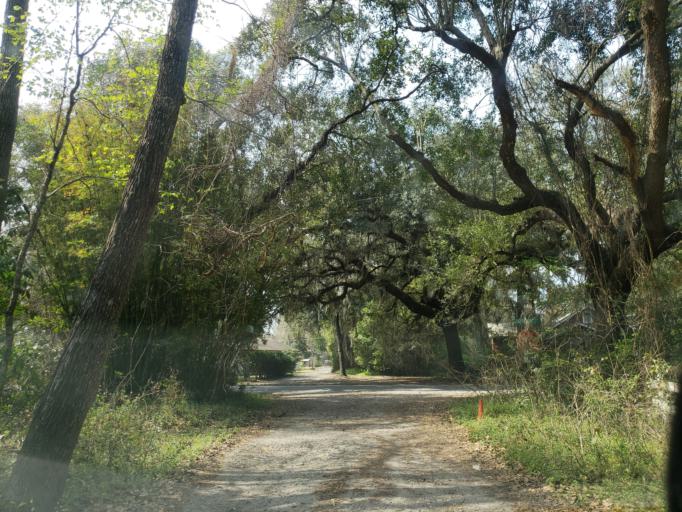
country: US
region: Georgia
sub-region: Chatham County
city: Isle of Hope
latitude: 31.9821
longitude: -81.0768
